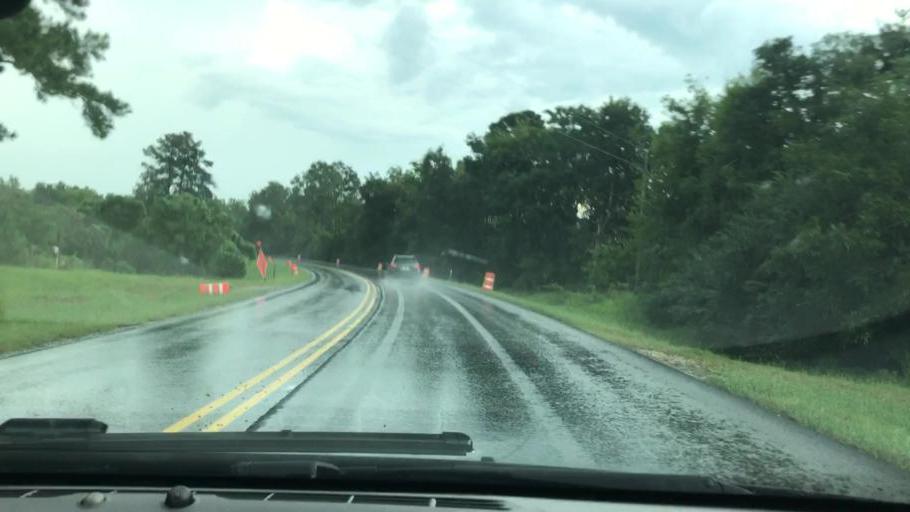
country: US
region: Georgia
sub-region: Clay County
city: Fort Gaines
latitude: 31.5650
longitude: -85.0180
